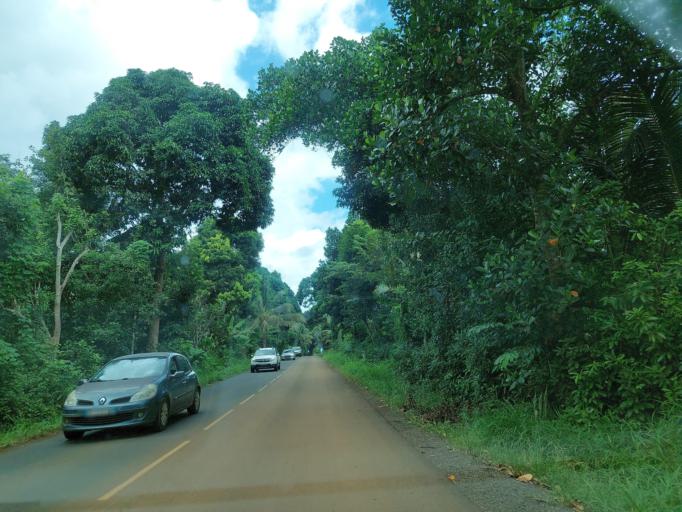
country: YT
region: M'Tsangamouji
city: M'Tsangamouji
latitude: -12.7505
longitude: 45.1149
